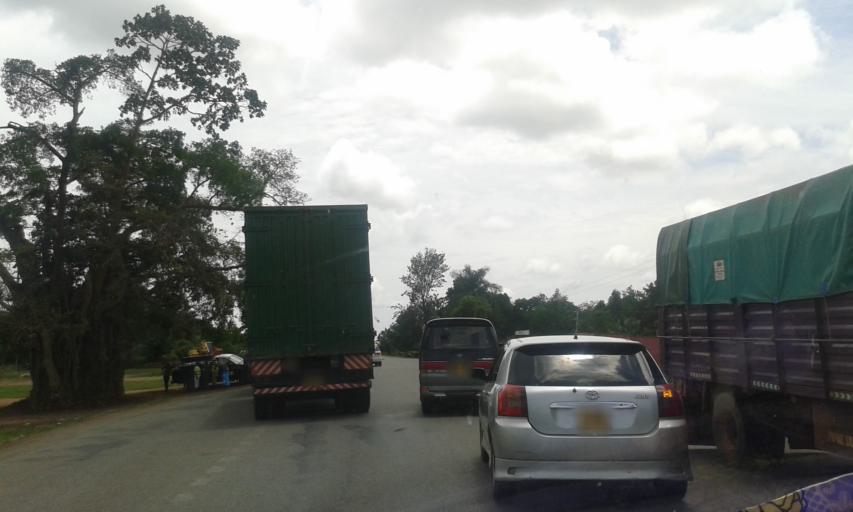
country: UG
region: Eastern Region
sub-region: Iganga District
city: Iganga
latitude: 0.5560
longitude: 33.4077
